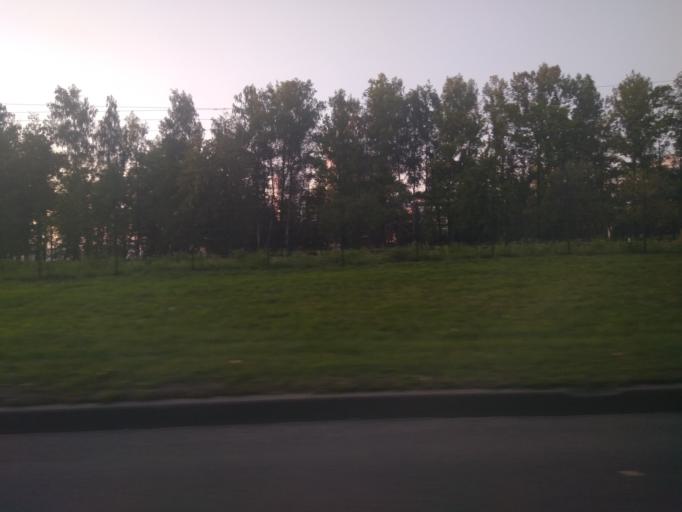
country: BY
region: Minsk
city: Zhdanovichy
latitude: 53.9303
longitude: 27.4711
